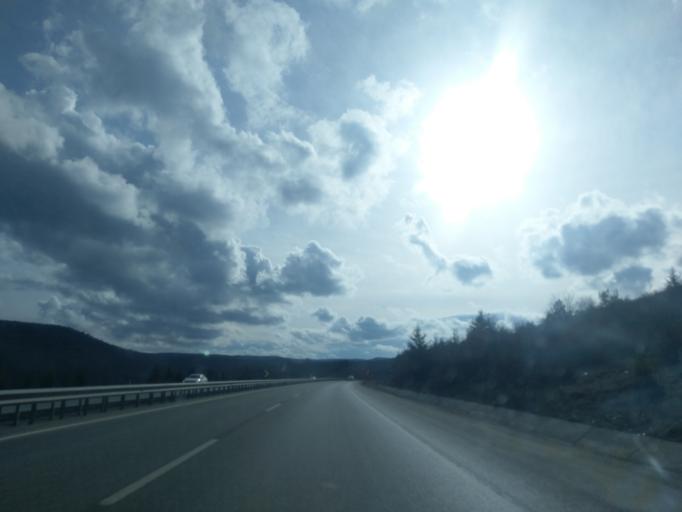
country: TR
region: Kuetahya
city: Sabuncu
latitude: 39.5976
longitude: 30.1441
